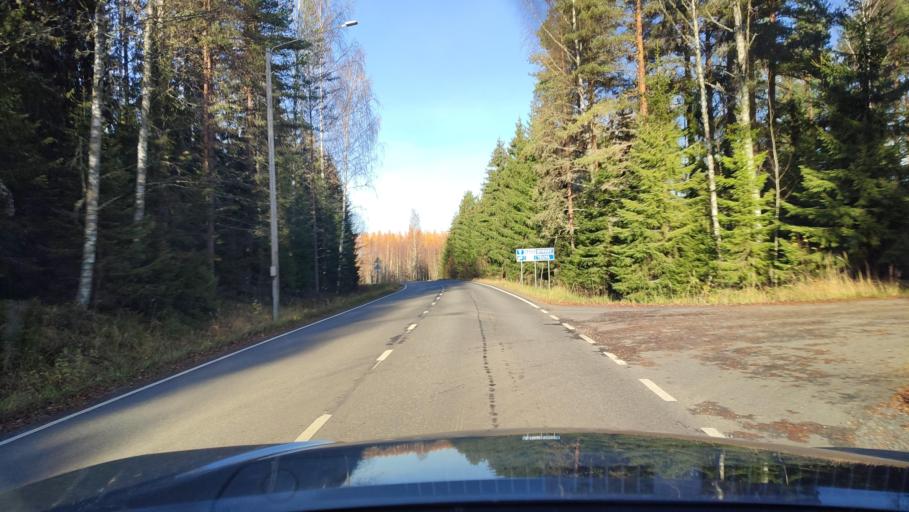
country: FI
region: Southern Ostrobothnia
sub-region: Suupohja
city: Karijoki
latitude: 62.3119
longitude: 21.7042
